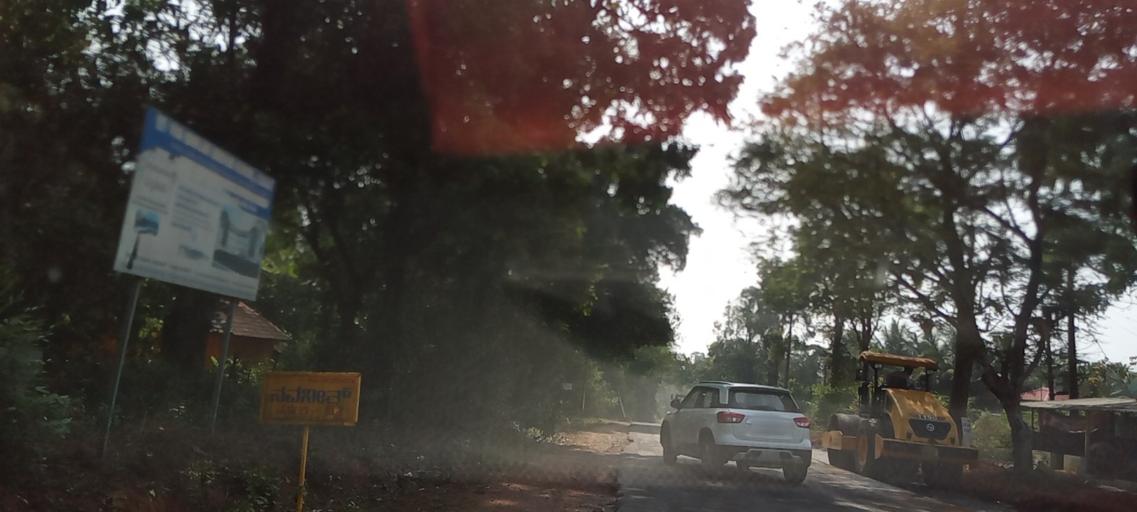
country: IN
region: Karnataka
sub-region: Udupi
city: Someshwar
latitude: 13.5309
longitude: 74.9191
